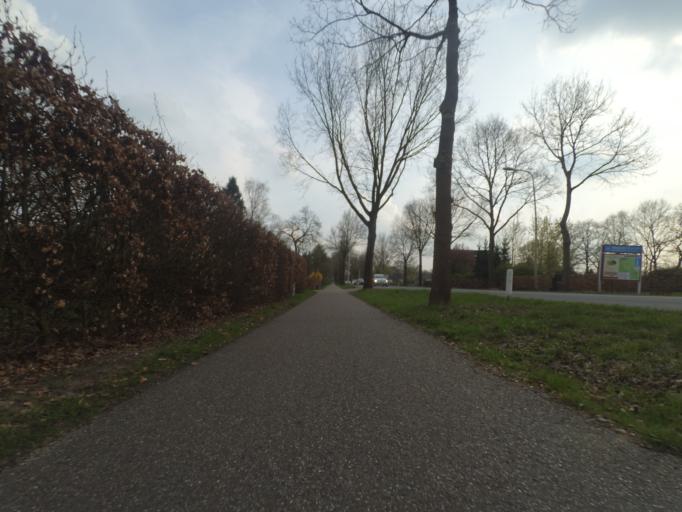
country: NL
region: Gelderland
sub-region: Gemeente Apeldoorn
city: Beekbergen
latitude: 52.1683
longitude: 5.9622
